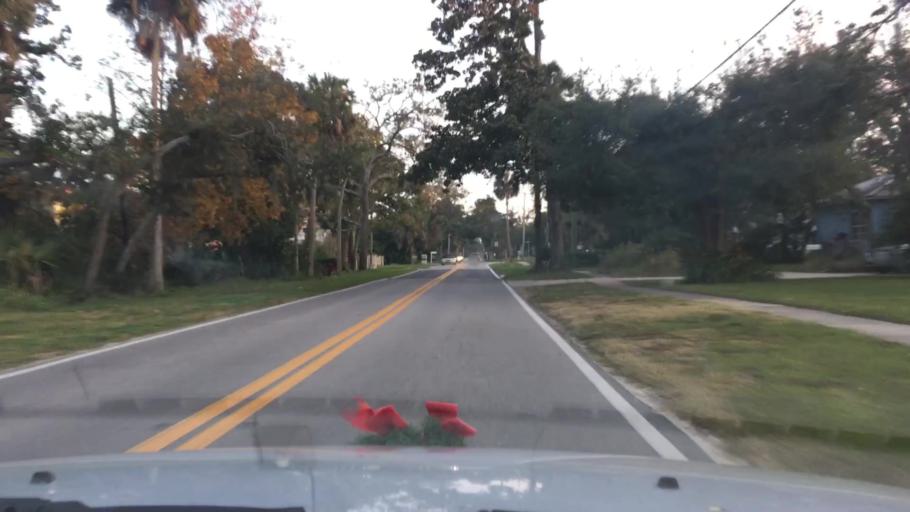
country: US
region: Florida
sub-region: Volusia County
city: Ormond Beach
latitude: 29.2959
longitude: -81.0603
